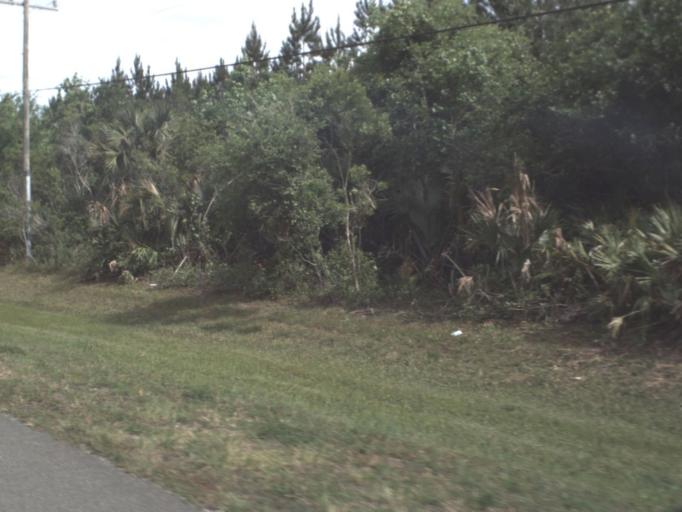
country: US
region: Florida
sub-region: Flagler County
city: Bunnell
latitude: 29.4677
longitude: -81.3031
